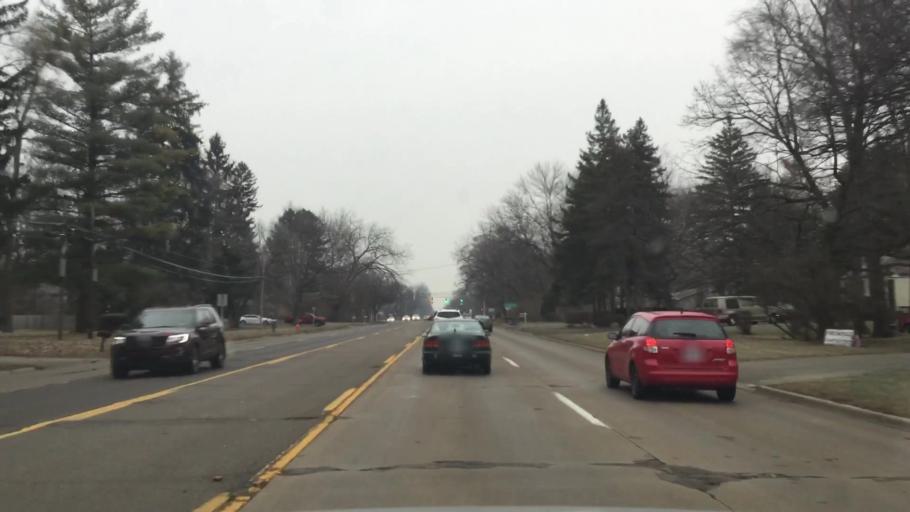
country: US
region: Michigan
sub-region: Wayne County
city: Livonia
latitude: 42.4099
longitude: -83.3546
